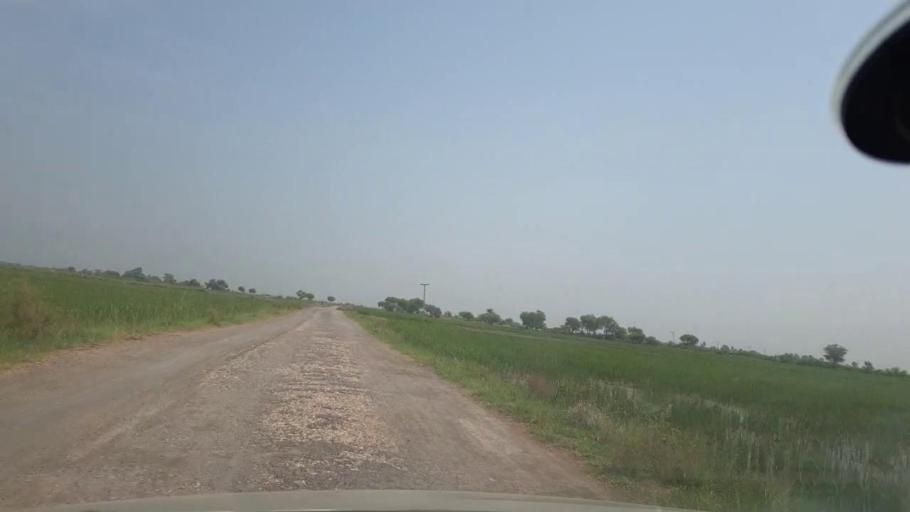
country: PK
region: Sindh
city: Jacobabad
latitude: 28.1387
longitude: 68.3695
